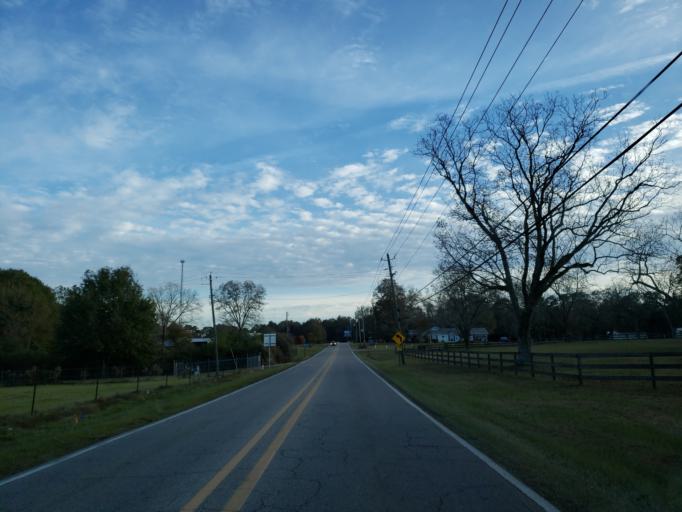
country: US
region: Mississippi
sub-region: Lamar County
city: Purvis
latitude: 31.1598
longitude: -89.4209
